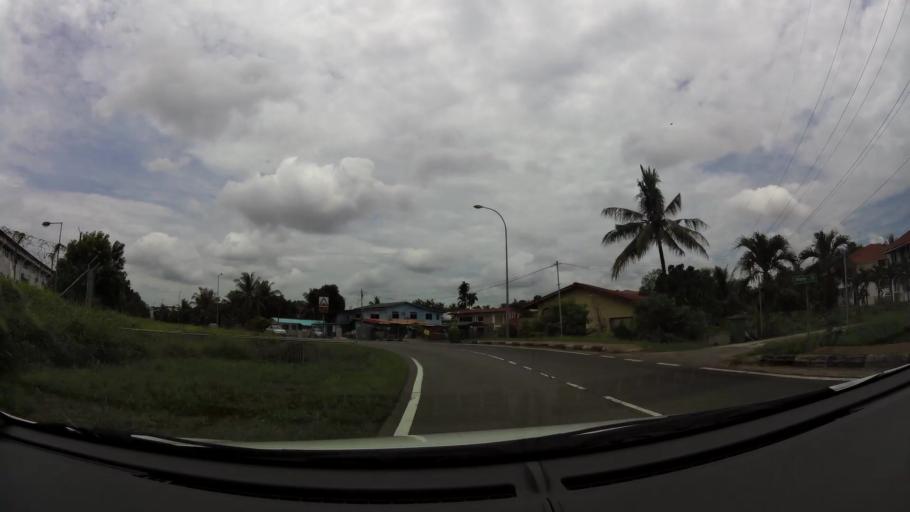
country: BN
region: Brunei and Muara
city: Bandar Seri Begawan
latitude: 4.9114
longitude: 114.9130
